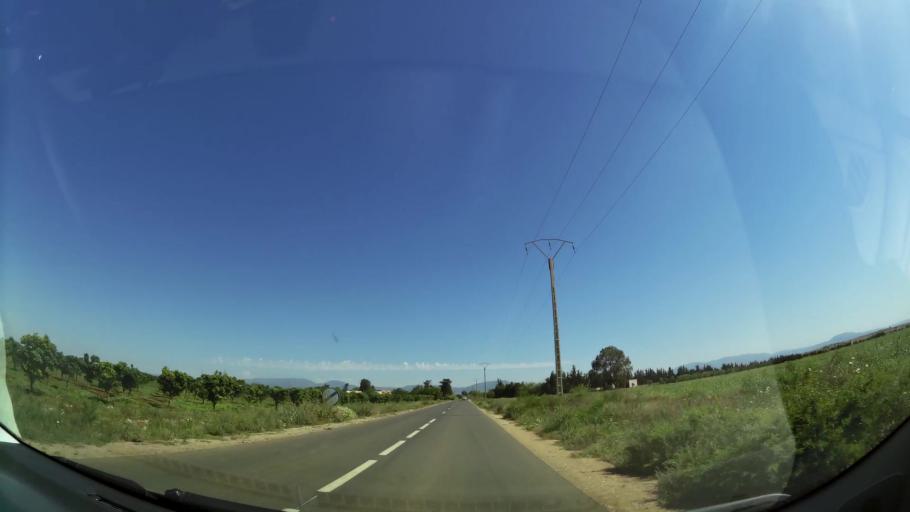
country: MA
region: Oriental
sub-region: Berkane-Taourirt
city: Madagh
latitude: 35.0214
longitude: -2.4087
